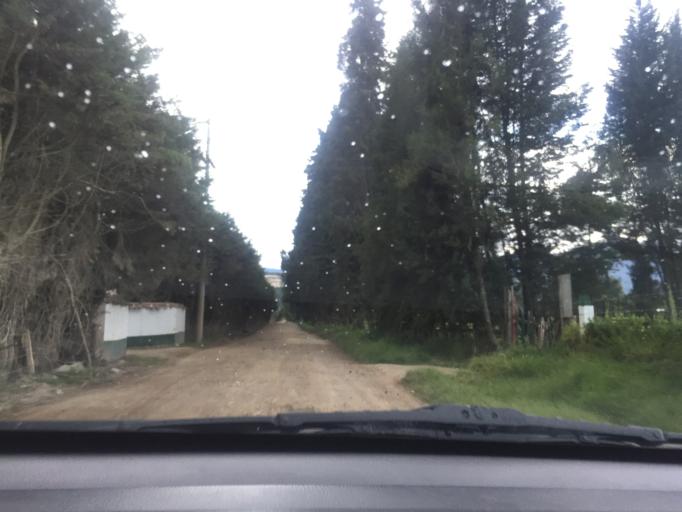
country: CO
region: Cundinamarca
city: Cogua
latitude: 5.0670
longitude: -73.9321
